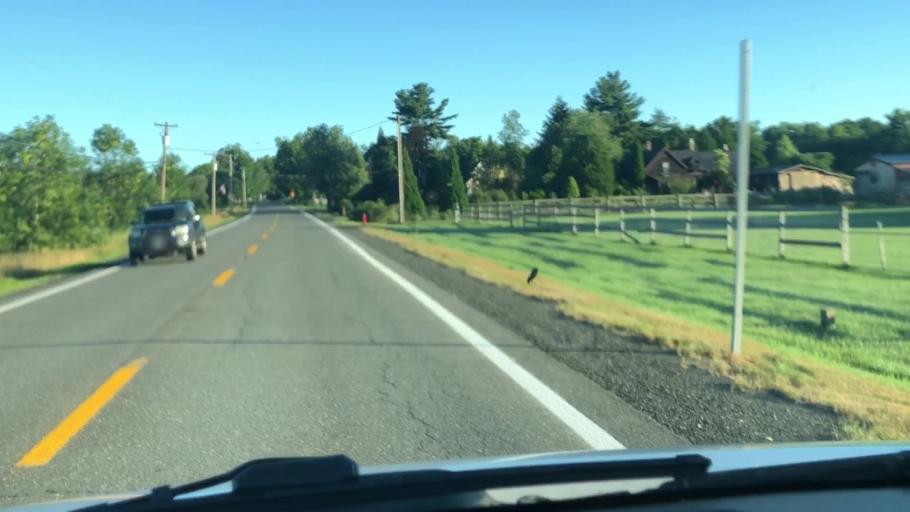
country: US
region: Massachusetts
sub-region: Hampshire County
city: Chesterfield
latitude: 42.3810
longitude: -72.9252
